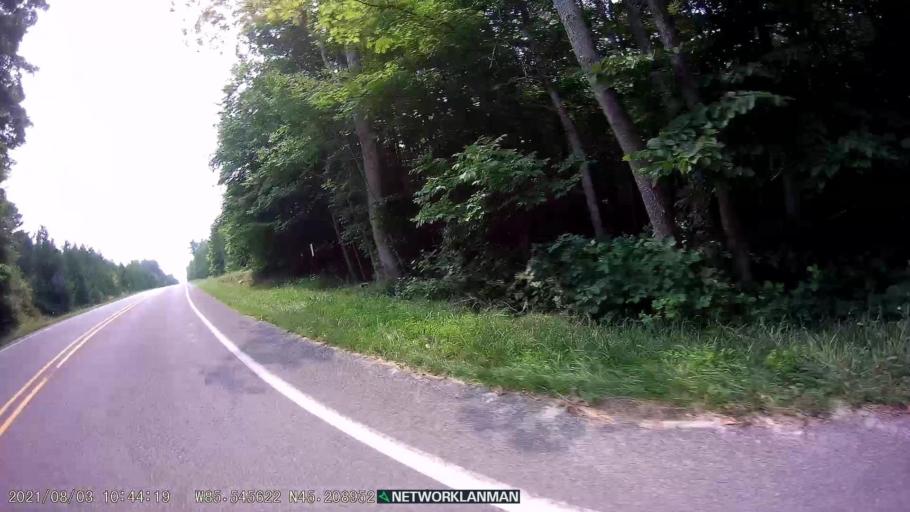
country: US
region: Michigan
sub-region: Leelanau County
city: Leland
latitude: 45.2089
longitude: -85.5456
